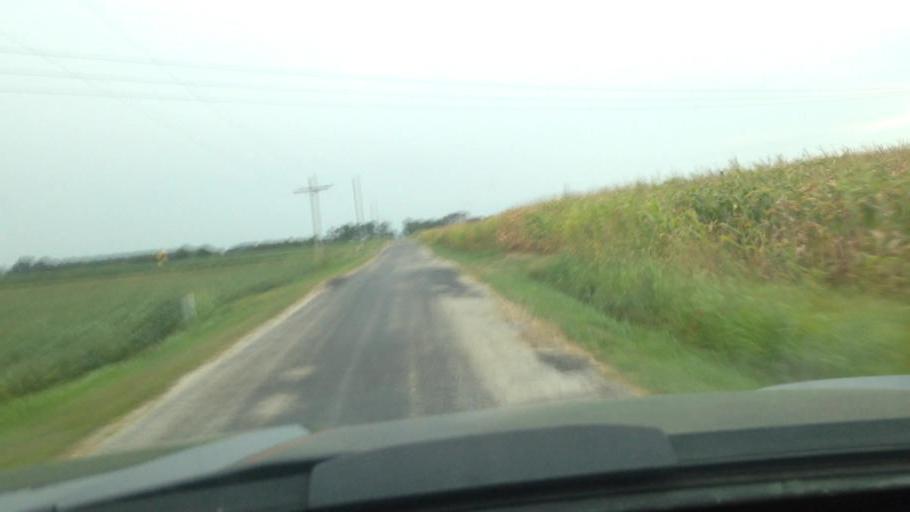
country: US
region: Indiana
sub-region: Randolph County
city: Union City
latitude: 40.2225
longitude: -84.8600
